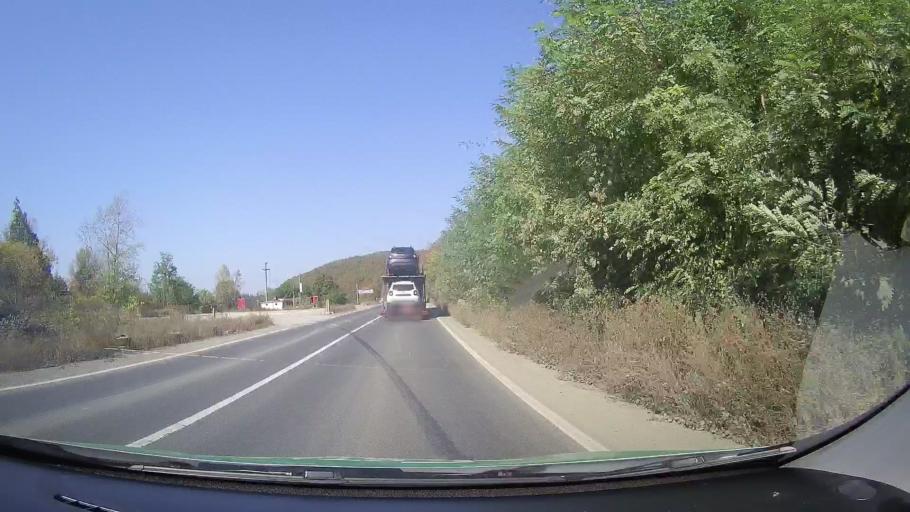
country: RO
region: Arad
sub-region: Comuna Bata
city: Bata
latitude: 46.0701
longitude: 22.0397
